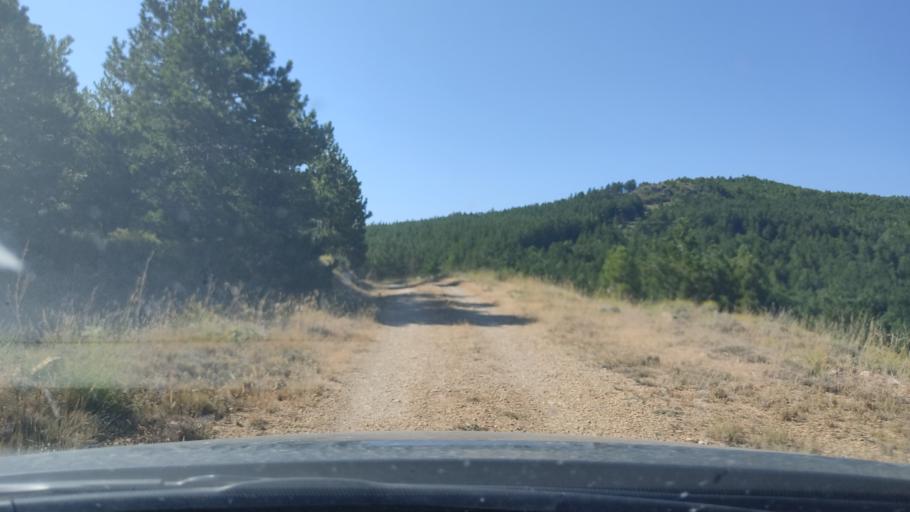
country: ES
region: Aragon
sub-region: Provincia de Teruel
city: Monforte de Moyuela
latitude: 41.0400
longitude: -1.0428
